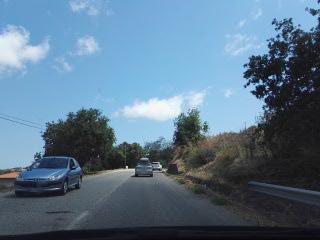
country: IT
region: Calabria
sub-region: Provincia di Vibo-Valentia
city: Ricadi
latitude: 38.6151
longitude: 15.8831
